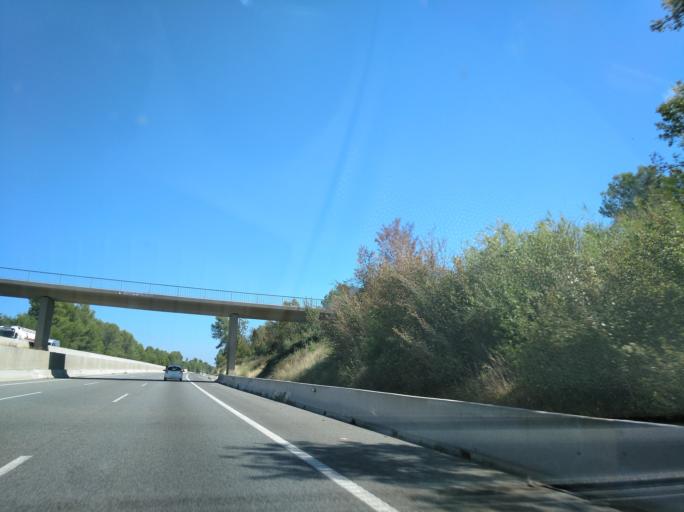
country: ES
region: Catalonia
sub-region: Provincia de Girona
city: Cervia de Ter
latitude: 42.0885
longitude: 2.8916
